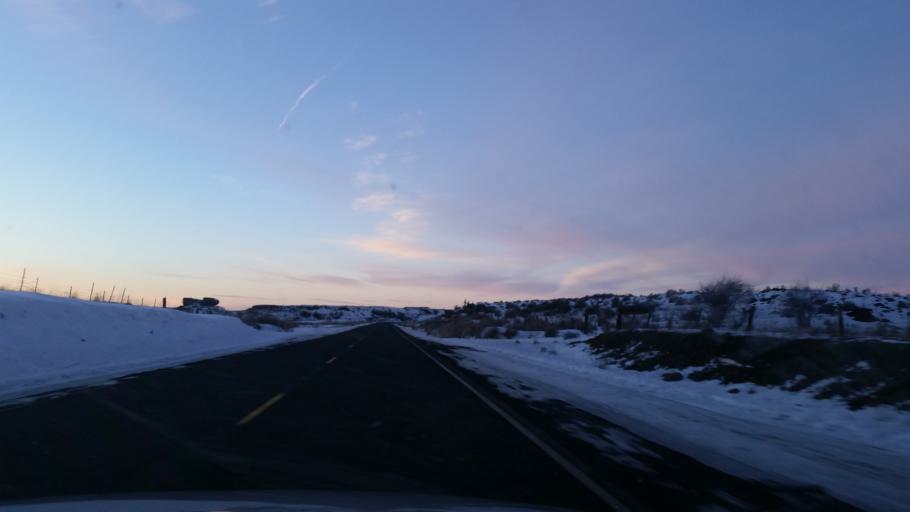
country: US
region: Washington
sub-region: Spokane County
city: Medical Lake
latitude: 47.2699
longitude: -117.9423
